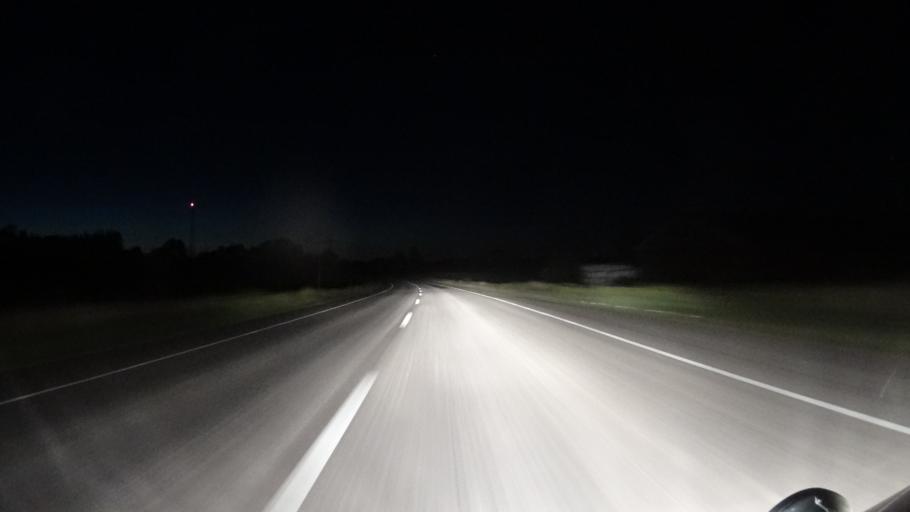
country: SE
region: OEstergoetland
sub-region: Odeshogs Kommun
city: OEdeshoeg
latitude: 58.2621
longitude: 14.7455
